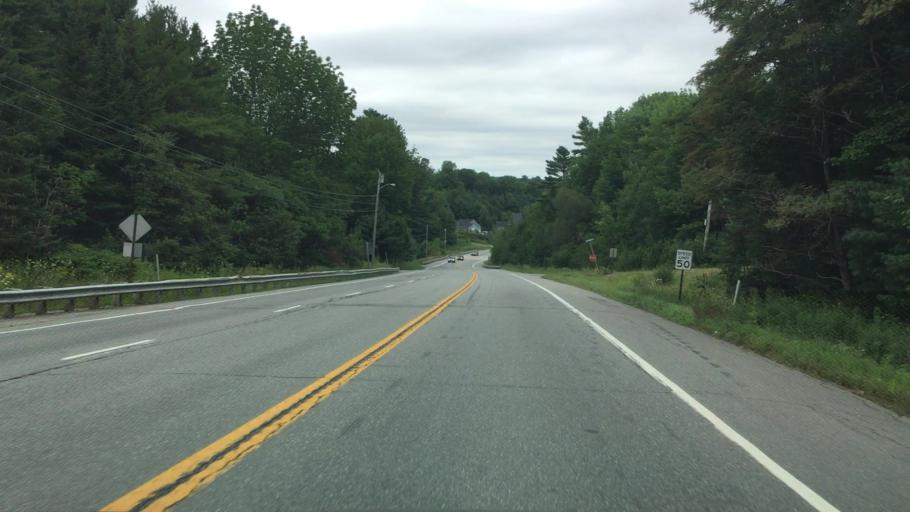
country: US
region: Maine
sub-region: Penobscot County
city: Orrington
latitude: 44.6918
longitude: -68.8477
